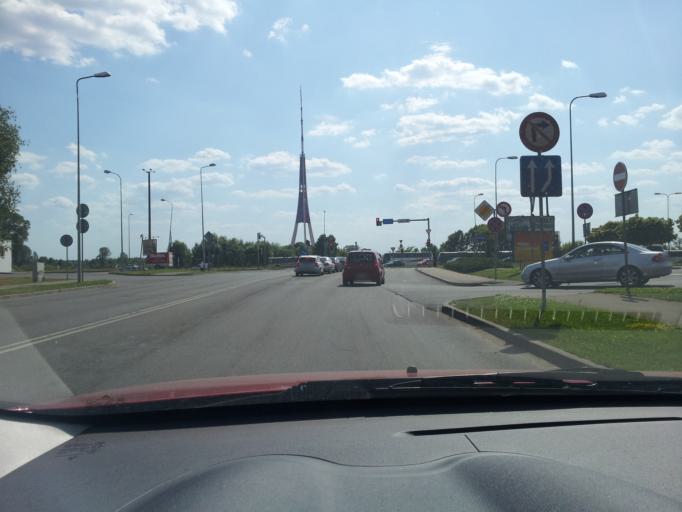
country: LV
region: Riga
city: Riga
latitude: 56.9343
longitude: 24.1454
